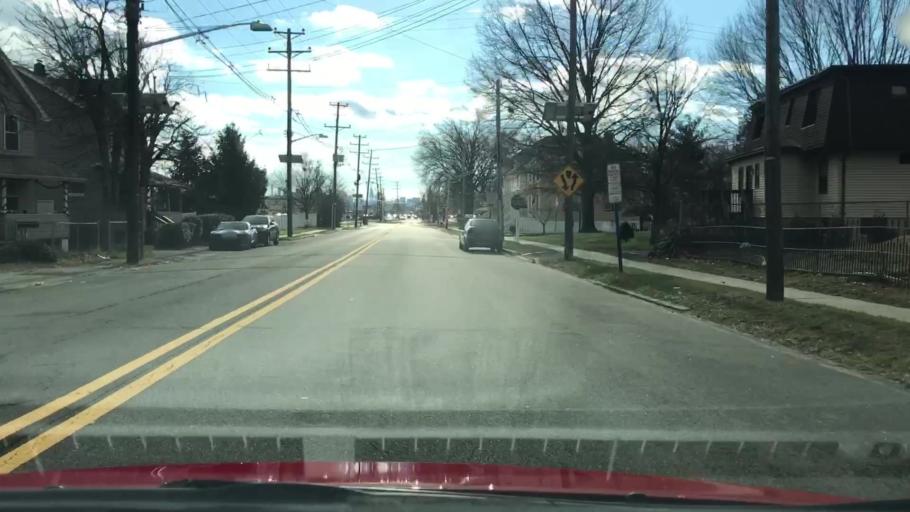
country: US
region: New Jersey
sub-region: Bergen County
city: Little Ferry
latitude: 40.8591
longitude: -74.0365
